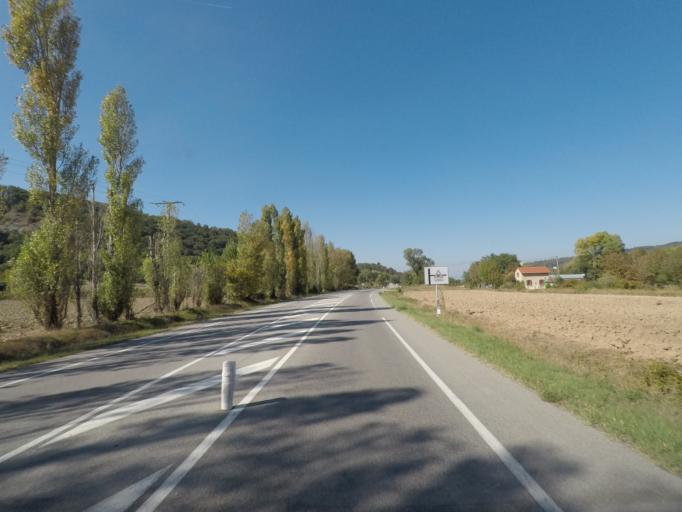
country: FR
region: Rhone-Alpes
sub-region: Departement de la Drome
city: Aouste-sur-Sye
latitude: 44.7154
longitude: 5.0428
